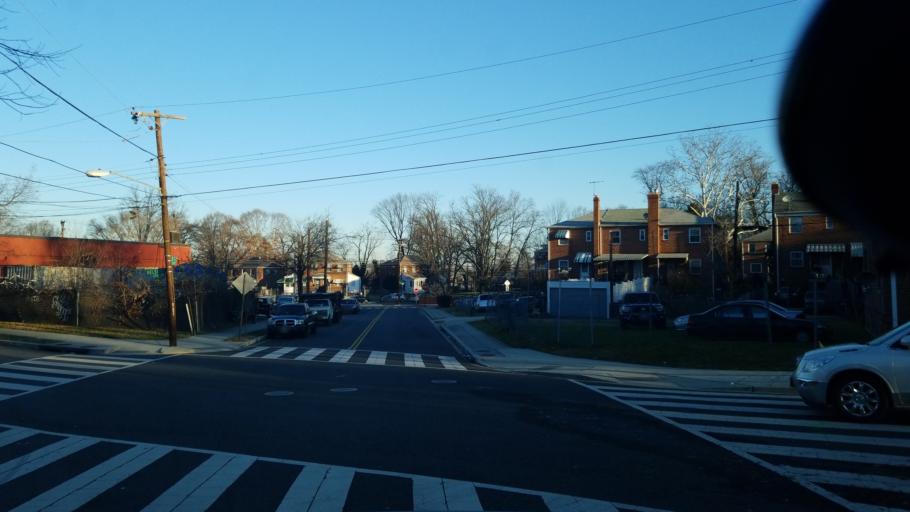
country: US
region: Maryland
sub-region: Prince George's County
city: Silver Hill
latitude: 38.8754
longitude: -76.9648
